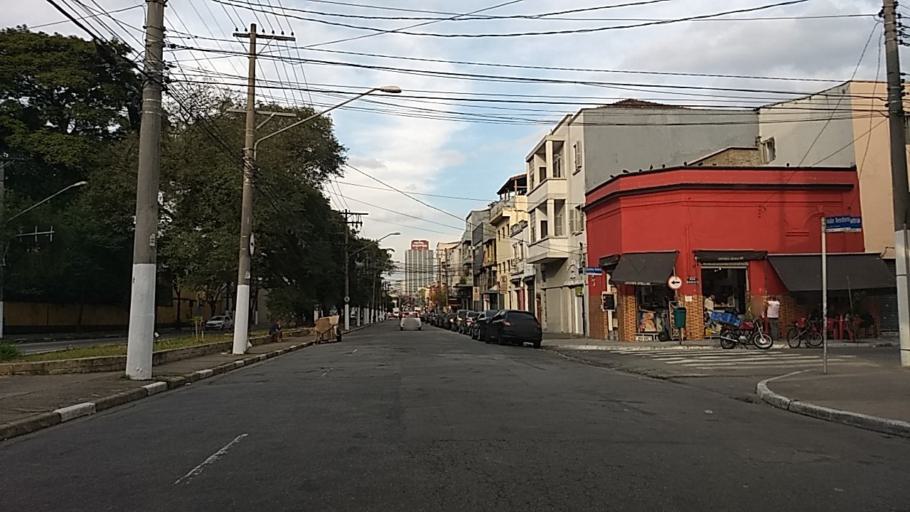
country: BR
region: Sao Paulo
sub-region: Sao Paulo
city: Sao Paulo
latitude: -23.5334
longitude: -46.6288
